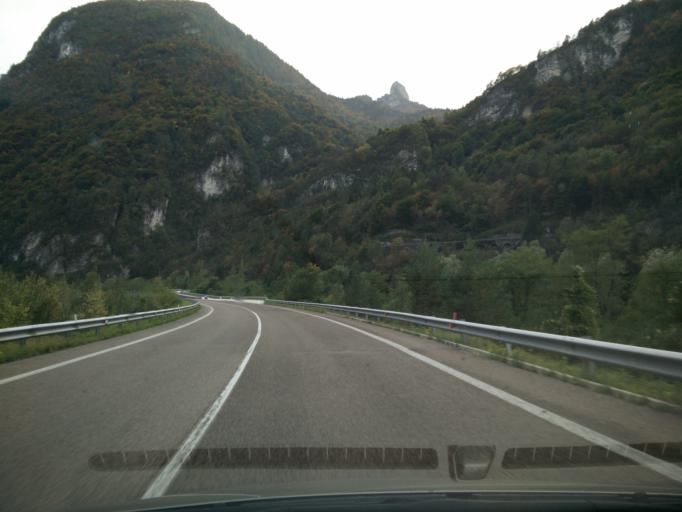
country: IT
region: Veneto
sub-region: Provincia di Belluno
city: Ospitale di Cadore
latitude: 46.3231
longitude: 12.3187
